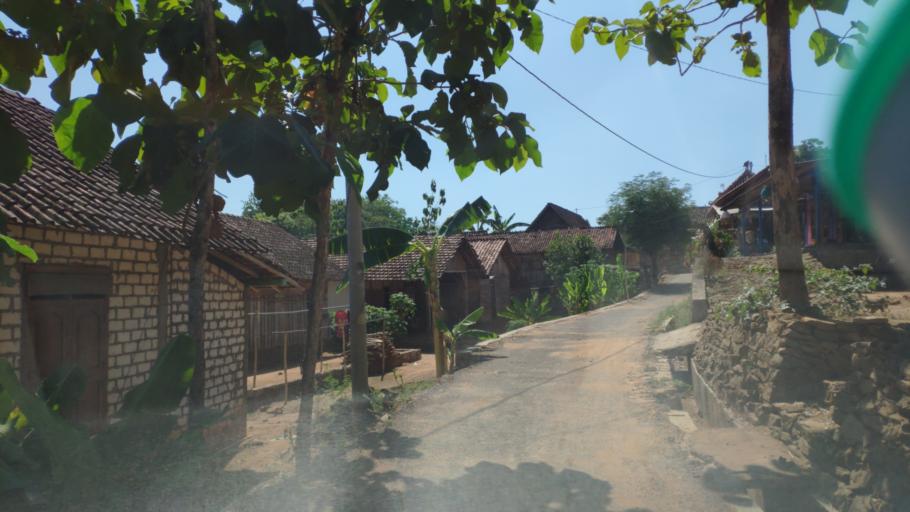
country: ID
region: East Java
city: Krajan Jamprong
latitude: -6.9808
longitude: 111.6190
